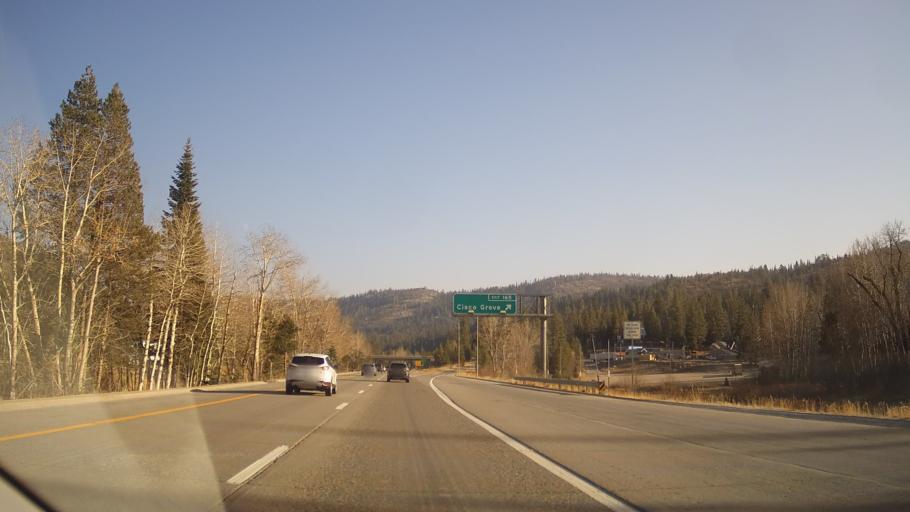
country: US
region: California
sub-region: Nevada County
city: Truckee
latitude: 39.3120
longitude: -120.5482
